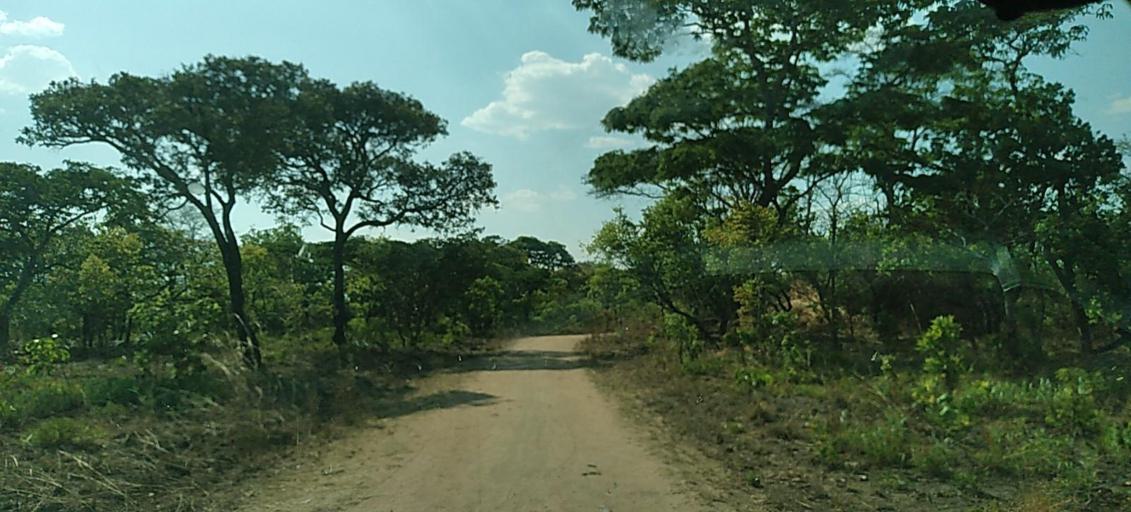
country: ZM
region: North-Western
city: Kalengwa
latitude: -13.1037
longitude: 24.9878
